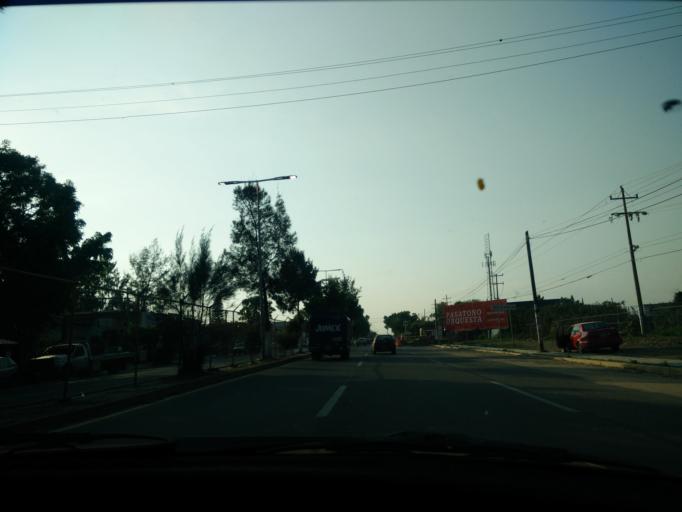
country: MX
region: Oaxaca
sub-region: Santa Maria Atzompa
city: San Jeronimo Yahuiche
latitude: 17.1188
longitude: -96.7612
